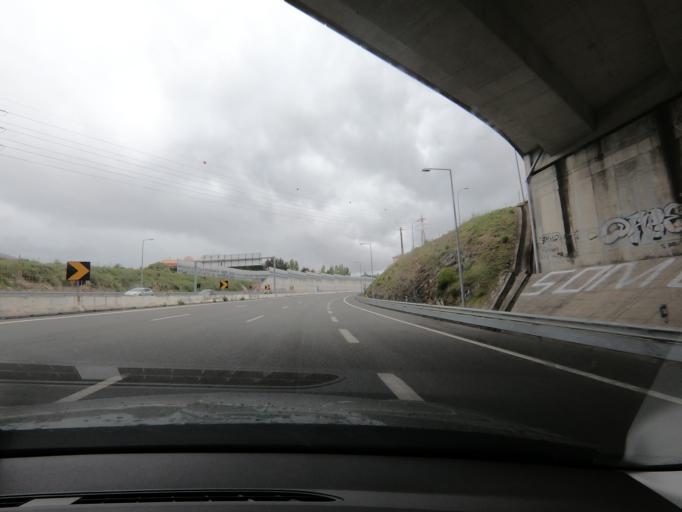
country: PT
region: Lisbon
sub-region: Cascais
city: Alcabideche
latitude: 38.7559
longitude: -9.3870
